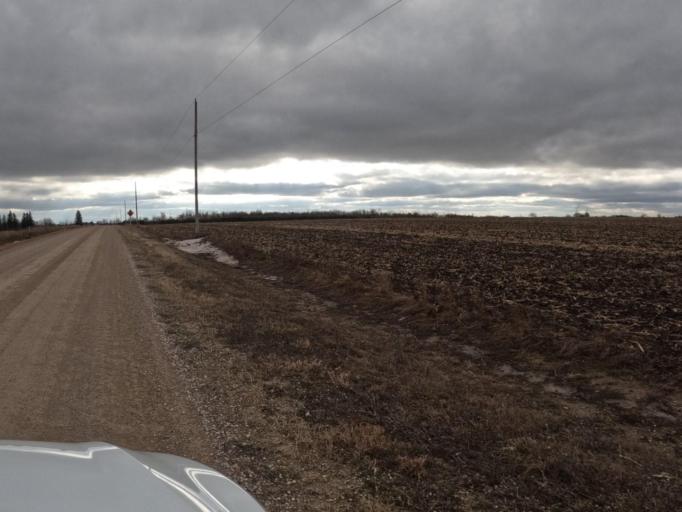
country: CA
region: Ontario
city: Shelburne
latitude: 43.8643
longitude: -80.3774
